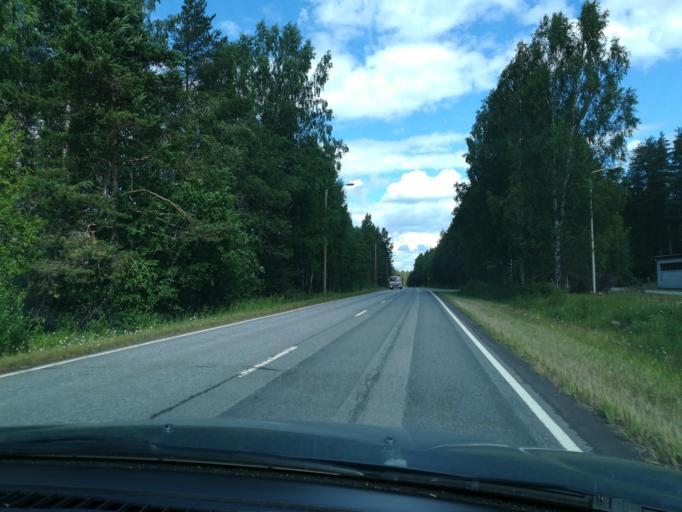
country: FI
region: Southern Savonia
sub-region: Mikkeli
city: Maentyharju
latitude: 61.4398
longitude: 26.8738
